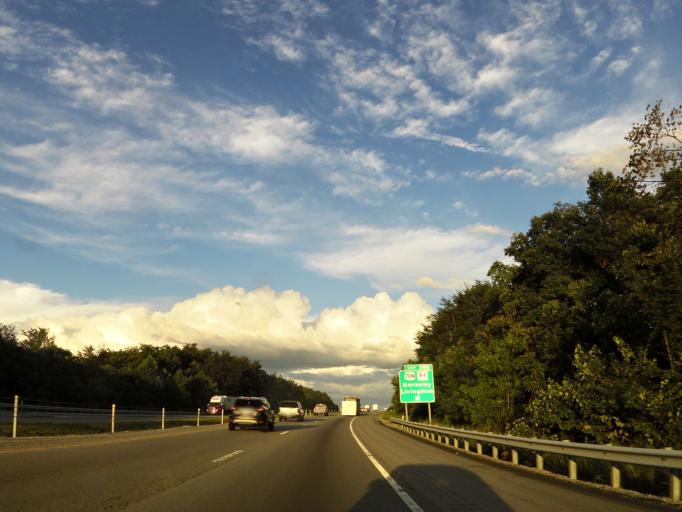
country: US
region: Tennessee
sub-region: Putnam County
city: Monterey
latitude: 36.1405
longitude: -85.2911
